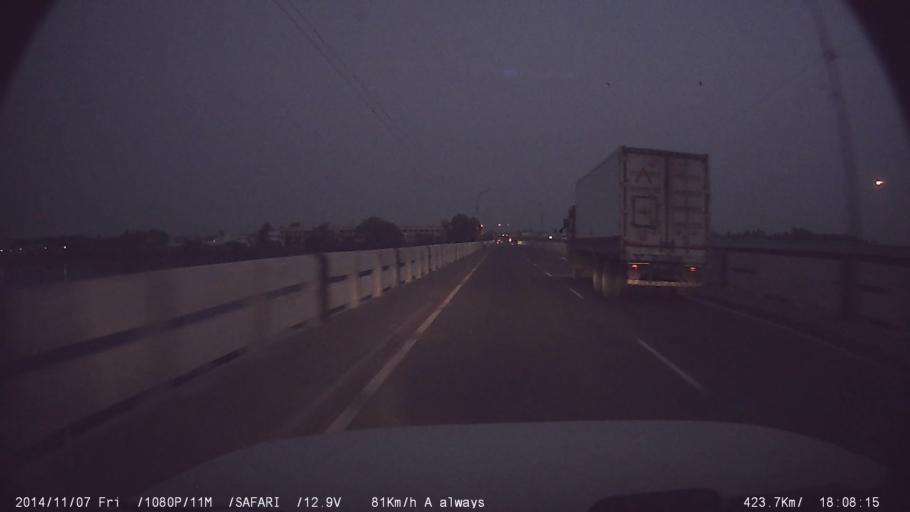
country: IN
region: Tamil Nadu
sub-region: Erode
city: Bhavani
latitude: 11.4319
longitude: 77.6845
